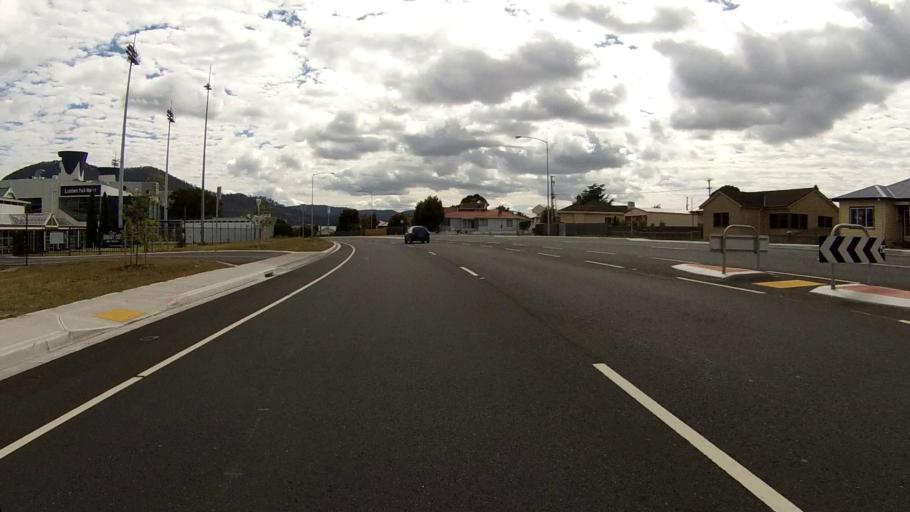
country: AU
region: Tasmania
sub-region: Glenorchy
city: Goodwood
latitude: -42.8266
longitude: 147.2882
